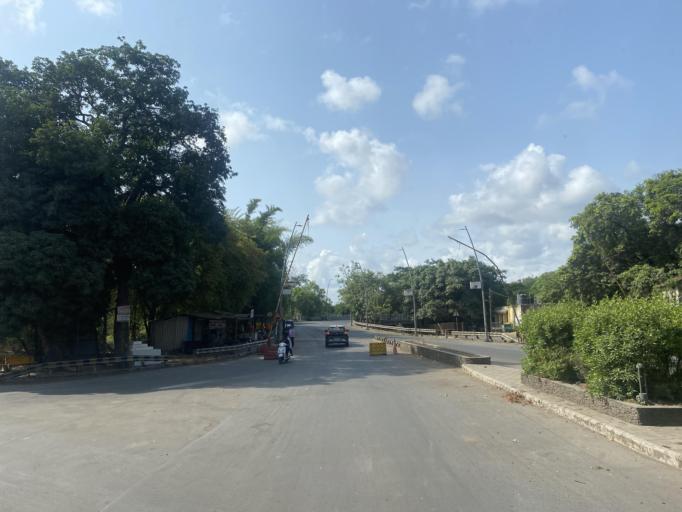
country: IN
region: Daman and Diu
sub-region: Daman District
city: Daman
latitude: 20.3752
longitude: 72.8502
